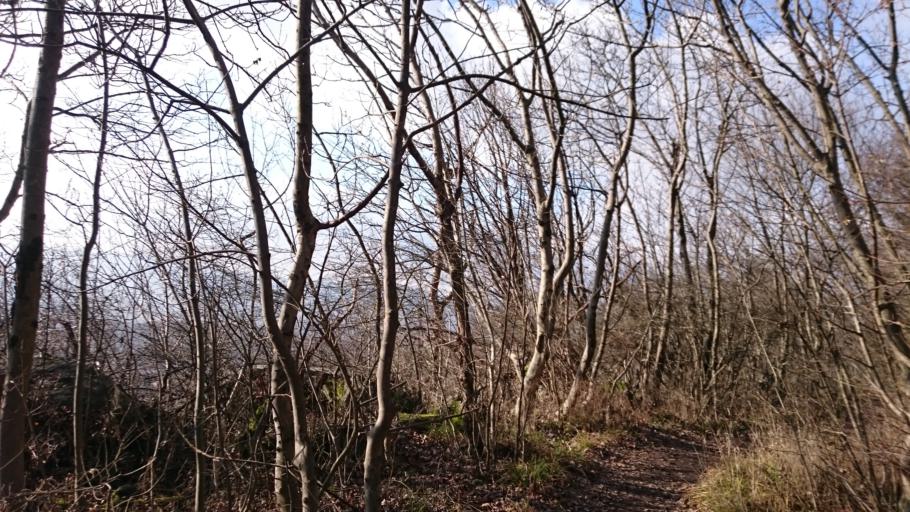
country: HU
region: Pest
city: Pilisborosjeno
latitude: 47.6141
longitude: 18.9990
